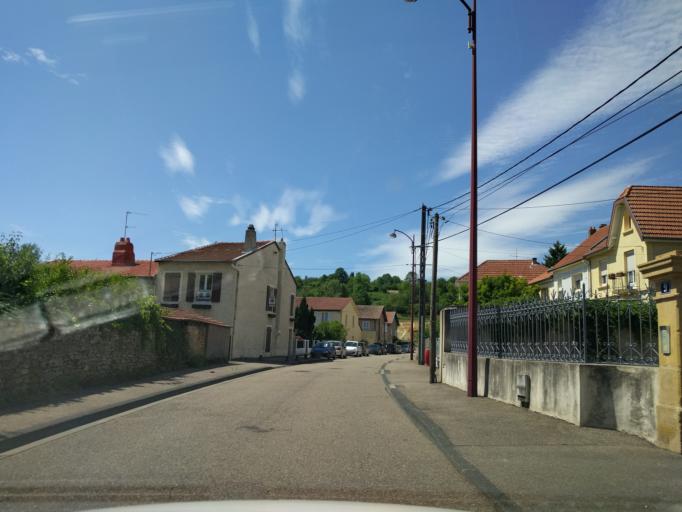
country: FR
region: Lorraine
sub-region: Departement de la Moselle
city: Le Ban Saint-Martin
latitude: 49.1326
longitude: 6.1488
